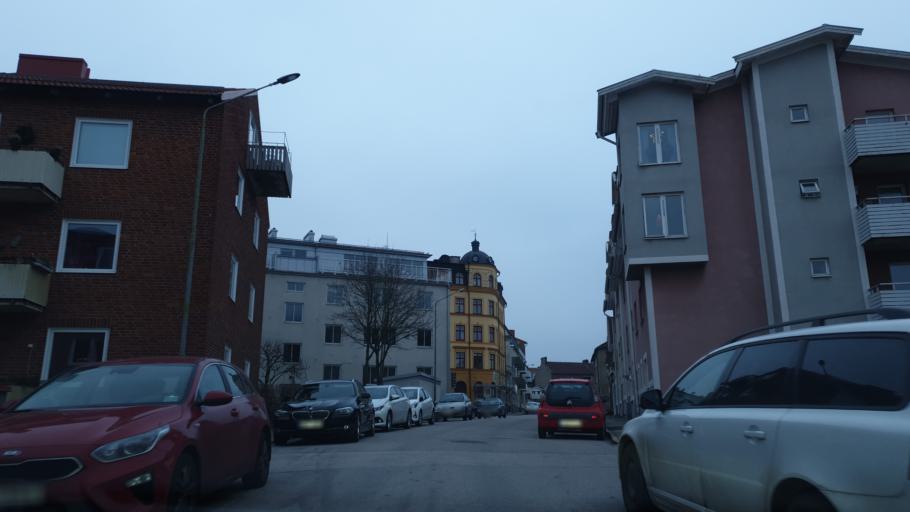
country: SE
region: Blekinge
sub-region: Karlskrona Kommun
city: Karlskrona
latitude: 56.1611
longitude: 15.5776
